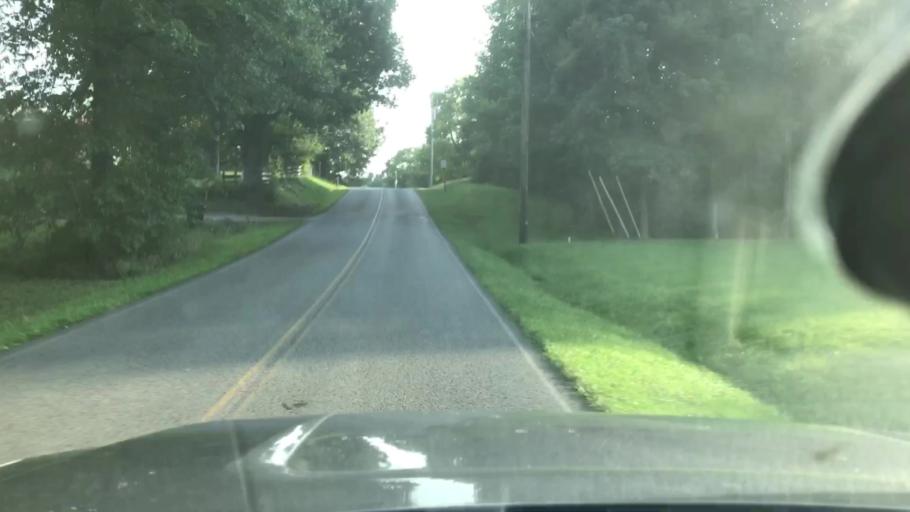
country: US
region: Tennessee
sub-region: Sumner County
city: Gallatin
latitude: 36.4787
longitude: -86.4684
